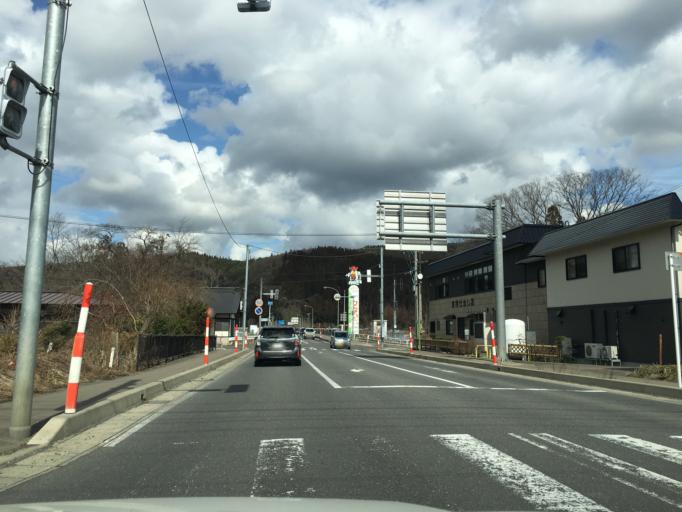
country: JP
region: Akita
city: Odate
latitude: 40.2258
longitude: 140.5899
